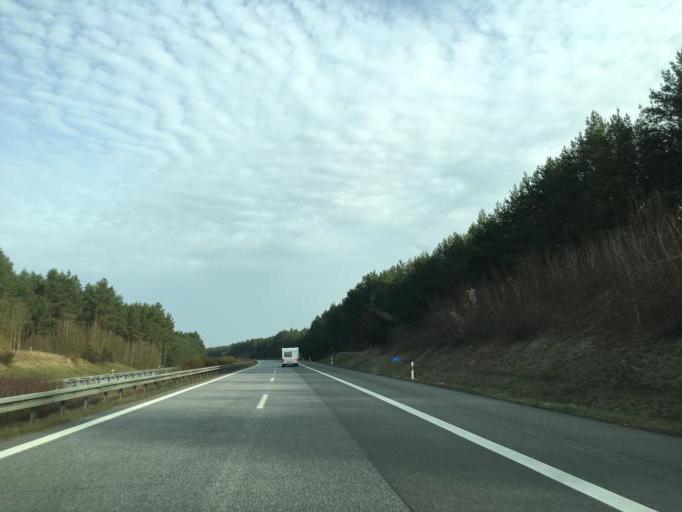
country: DE
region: Mecklenburg-Vorpommern
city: Malchow
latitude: 53.5264
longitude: 12.3538
